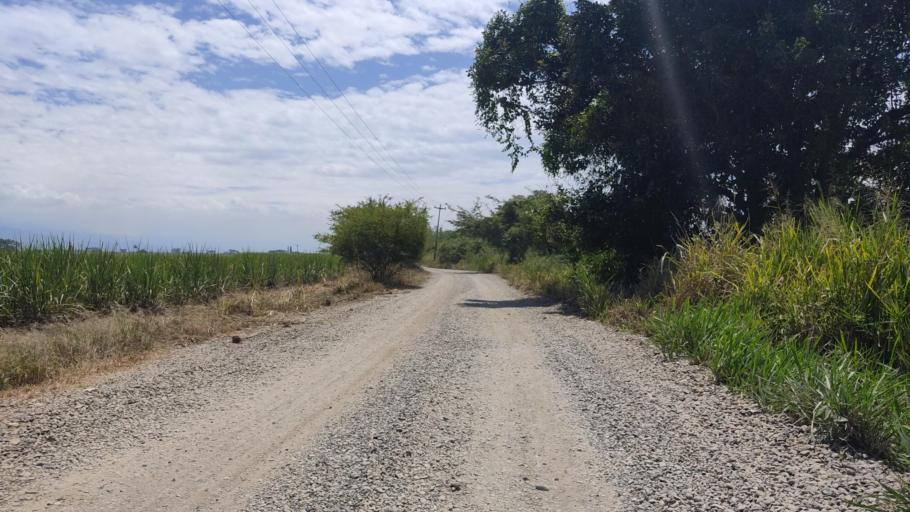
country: CO
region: Valle del Cauca
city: Jamundi
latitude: 3.1581
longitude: -76.5124
